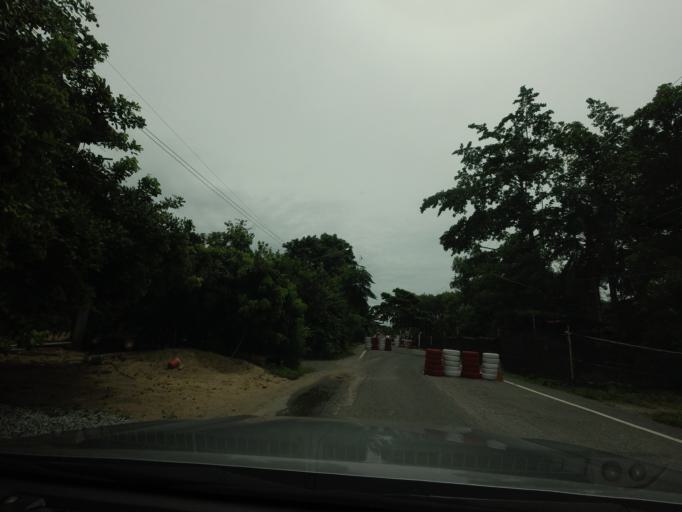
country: TH
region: Pattani
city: Kapho
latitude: 6.6338
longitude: 101.5488
